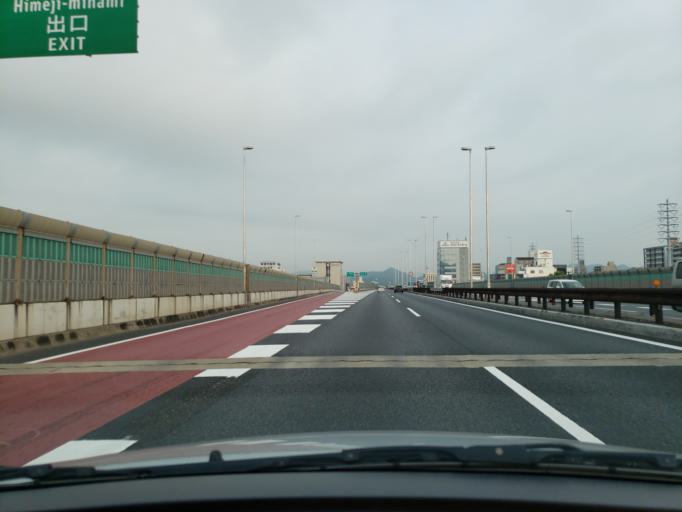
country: JP
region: Hyogo
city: Himeji
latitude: 34.8102
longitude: 134.6871
